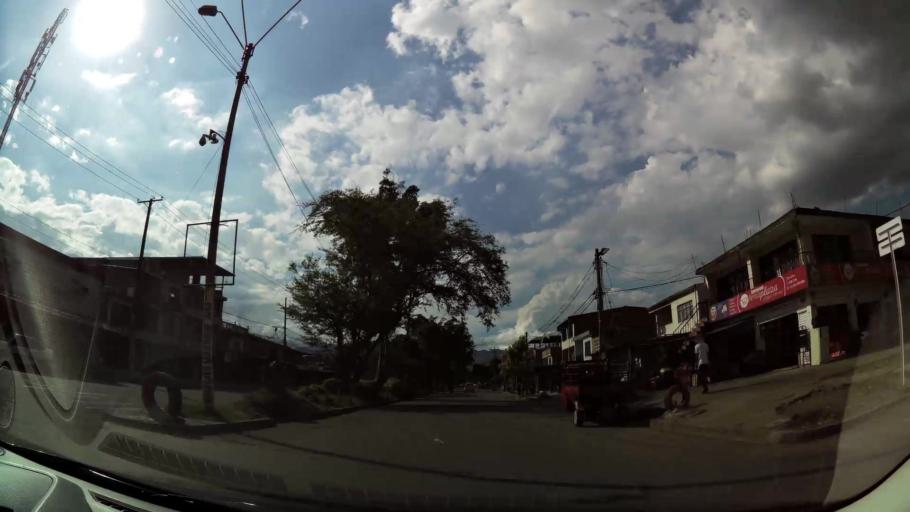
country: CO
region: Valle del Cauca
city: Cali
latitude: 3.4160
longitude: -76.5047
